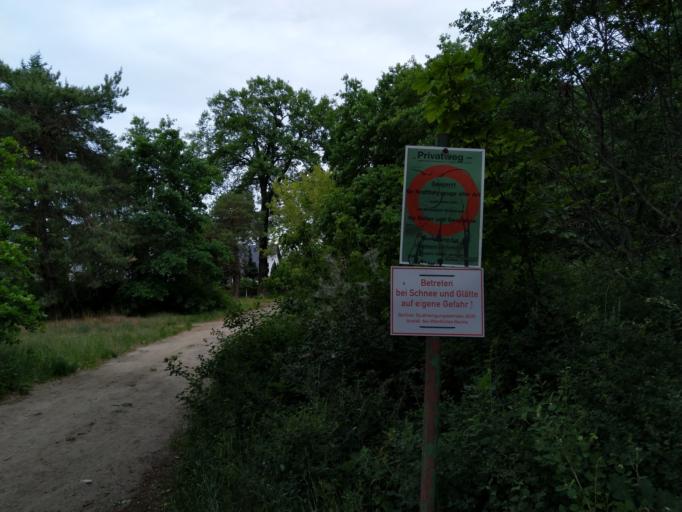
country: DE
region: Berlin
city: Kopenick Bezirk
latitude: 52.4702
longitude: 13.5777
